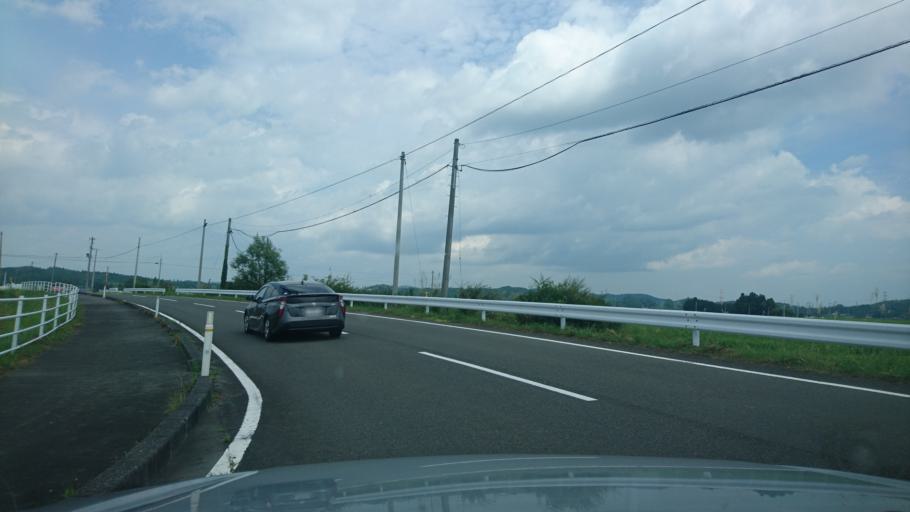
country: JP
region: Iwate
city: Ichinoseki
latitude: 38.8101
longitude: 140.9515
